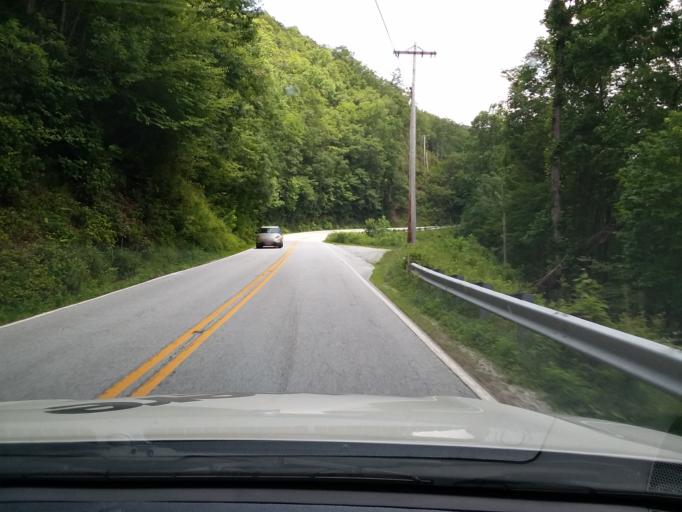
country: US
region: Georgia
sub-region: Rabun County
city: Mountain City
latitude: 35.0320
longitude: -83.2682
